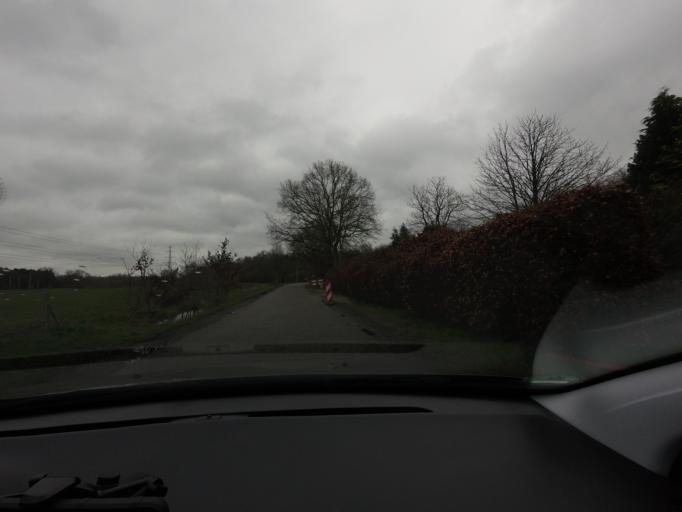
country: NL
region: Drenthe
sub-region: Gemeente Hoogeveen
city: Hoogeveen
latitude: 52.7726
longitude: 6.4954
